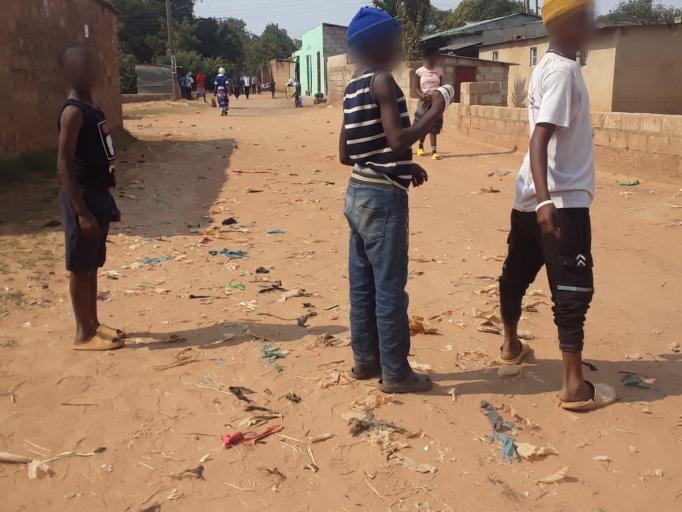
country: ZM
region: Lusaka
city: Lusaka
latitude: -15.3562
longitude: 28.2966
